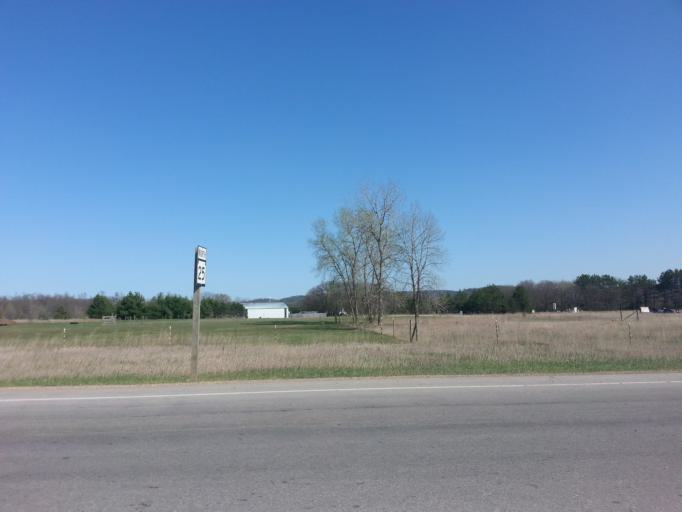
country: US
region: Wisconsin
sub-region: Pepin County
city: Durand
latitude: 44.6348
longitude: -91.9960
